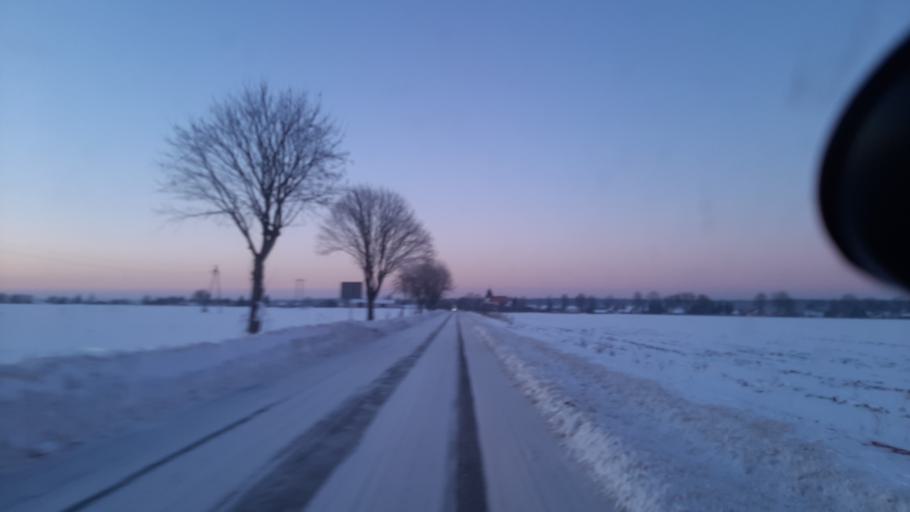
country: PL
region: Lublin Voivodeship
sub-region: Powiat lubelski
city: Niemce
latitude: 51.3556
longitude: 22.5353
